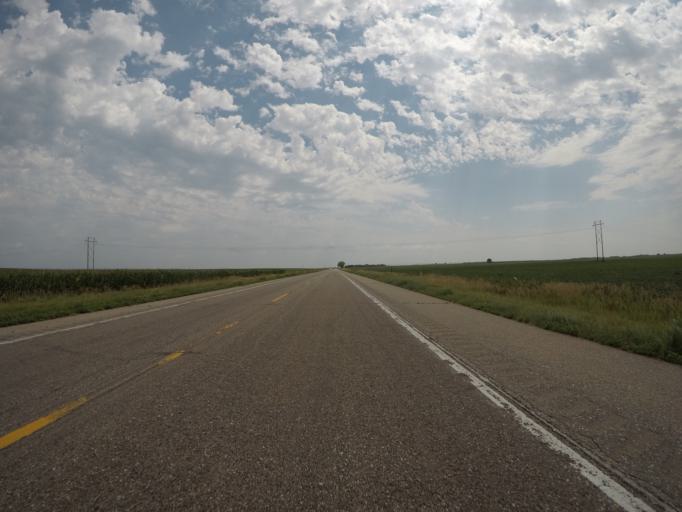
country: US
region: Nebraska
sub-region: Clay County
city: Clay Center
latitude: 40.5622
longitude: -98.0515
